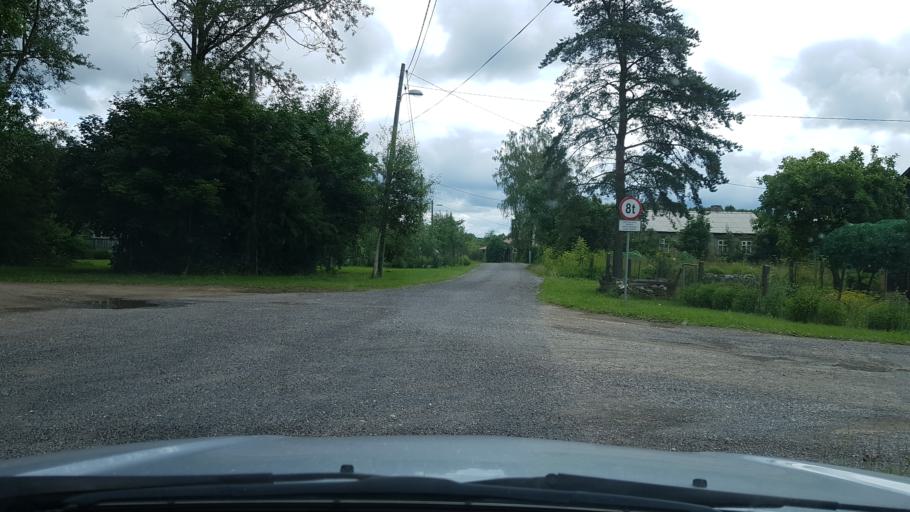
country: EE
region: Ida-Virumaa
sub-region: Sillamaee linn
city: Sillamae
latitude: 59.3724
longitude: 27.7677
